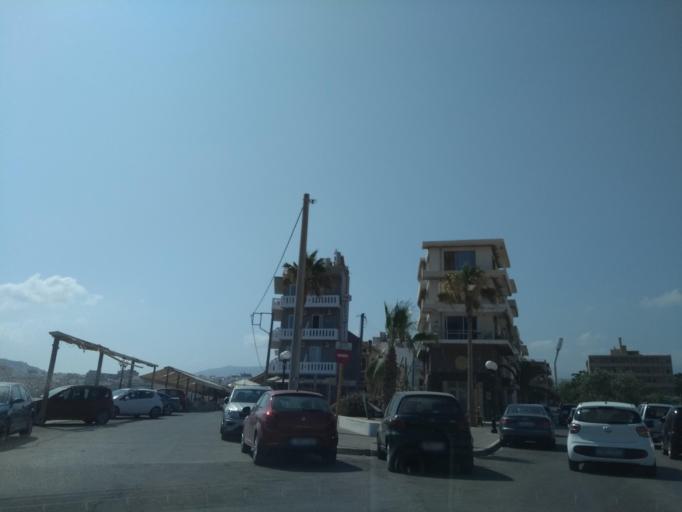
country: GR
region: Crete
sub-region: Nomos Chanias
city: Chania
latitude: 35.5174
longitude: 24.0244
